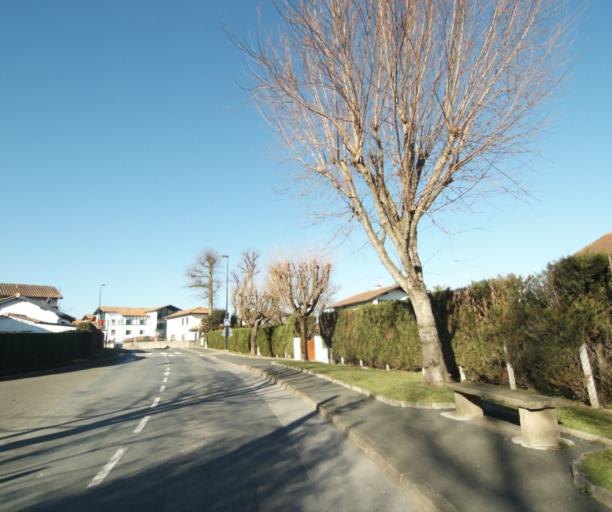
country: FR
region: Aquitaine
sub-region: Departement des Pyrenees-Atlantiques
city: Ciboure
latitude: 43.3762
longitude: -1.6703
